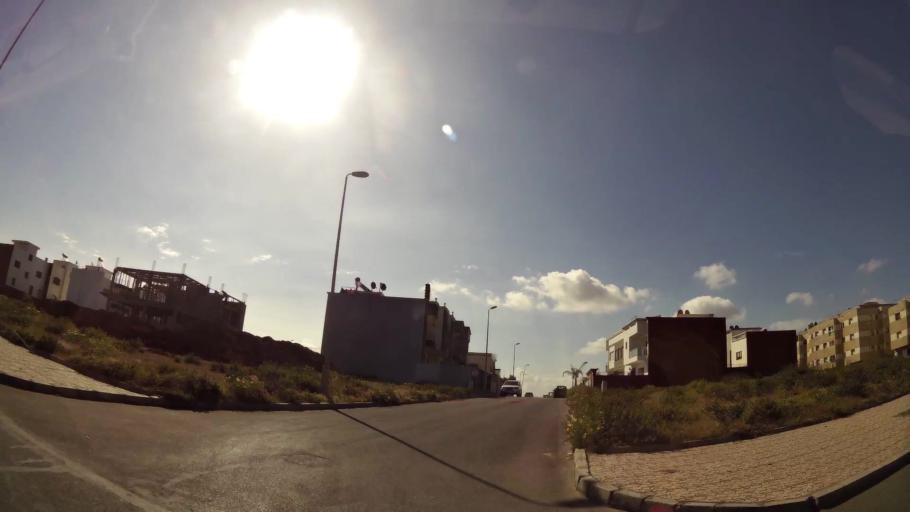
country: MA
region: Rabat-Sale-Zemmour-Zaer
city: Sale
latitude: 34.0666
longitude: -6.8068
